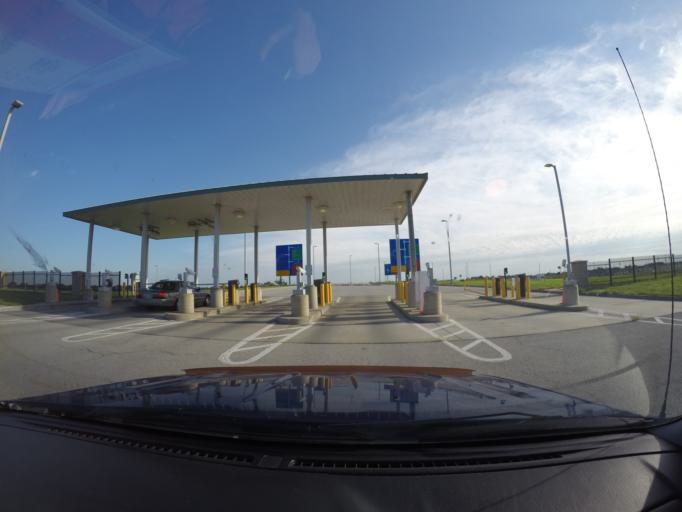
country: US
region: Missouri
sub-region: Platte County
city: Weatherby Lake
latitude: 39.3133
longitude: -94.7004
